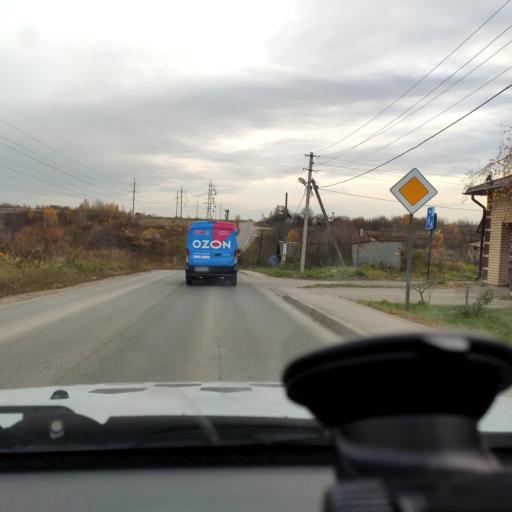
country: RU
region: Perm
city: Perm
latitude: 58.0129
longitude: 56.3229
